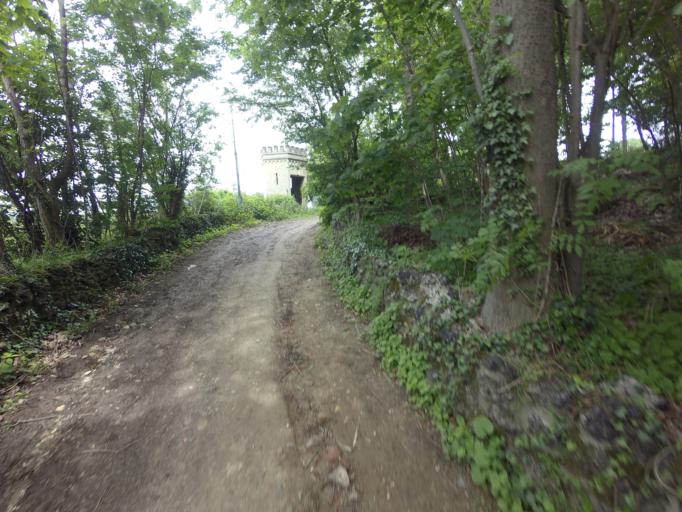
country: NL
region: Limburg
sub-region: Gemeente Maastricht
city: Heer
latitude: 50.8374
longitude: 5.7532
